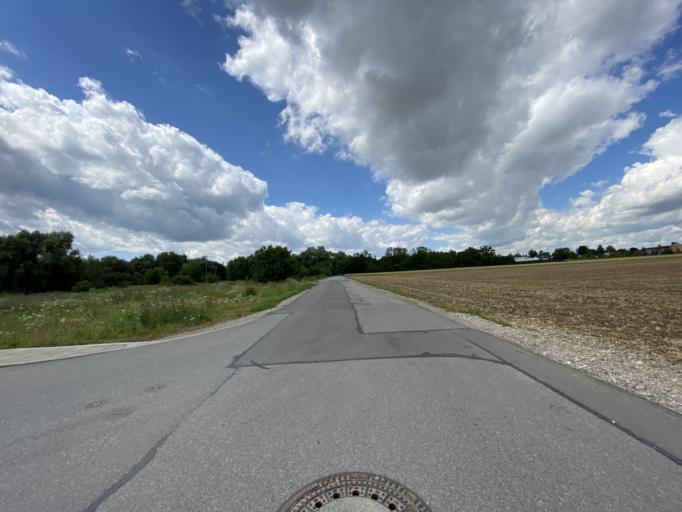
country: DE
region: Bavaria
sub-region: Upper Bavaria
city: Gilching
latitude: 48.1009
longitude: 11.3063
